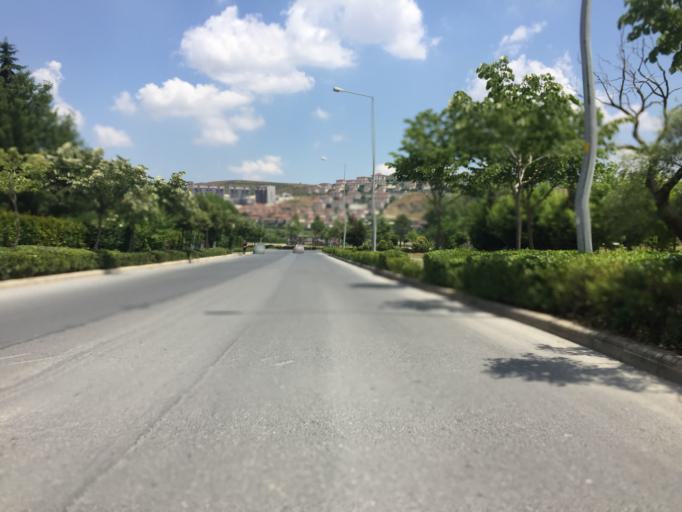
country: TR
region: Istanbul
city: Esenyurt
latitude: 41.0850
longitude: 28.6708
